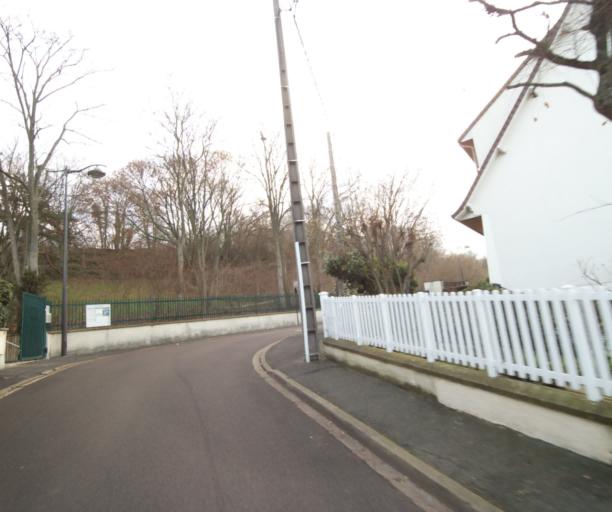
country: FR
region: Ile-de-France
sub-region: Departement des Hauts-de-Seine
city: Suresnes
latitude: 48.8708
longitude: 2.2098
